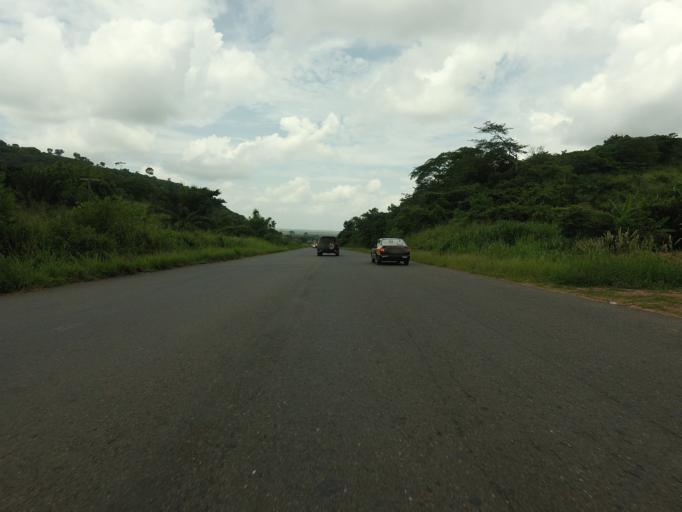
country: GH
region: Volta
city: Ho
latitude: 6.4264
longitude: 0.1688
